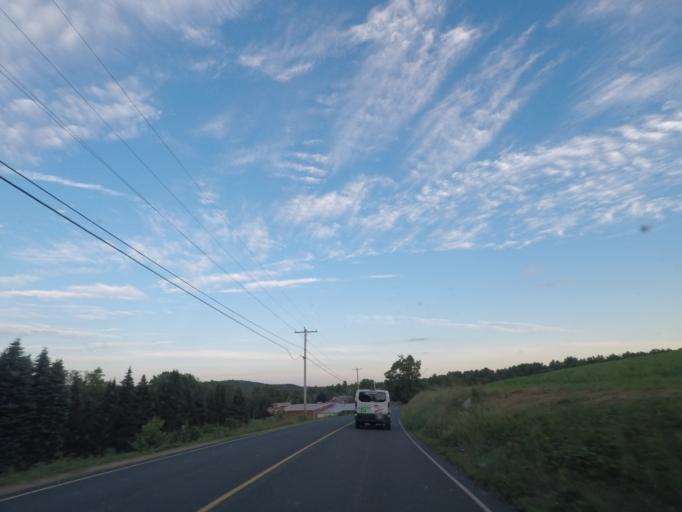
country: US
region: Massachusetts
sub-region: Worcester County
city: Fiskdale
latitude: 42.1605
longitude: -72.1455
